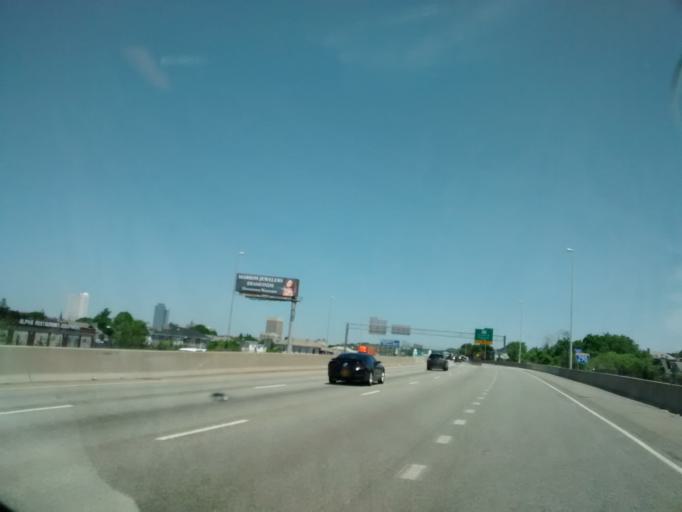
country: US
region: Massachusetts
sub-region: Worcester County
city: Worcester
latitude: 42.2470
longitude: -71.8012
